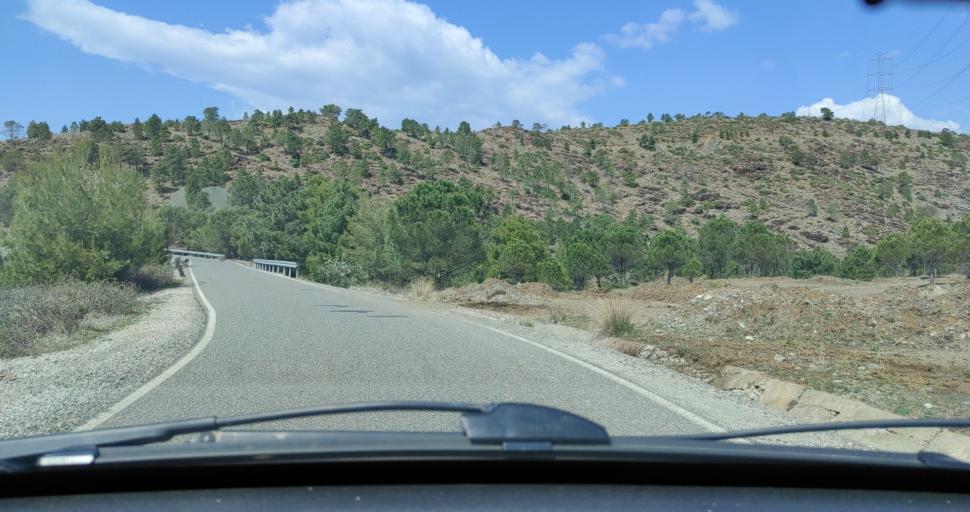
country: AL
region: Shkoder
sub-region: Rrethi i Shkodres
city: Hajmel
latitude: 41.9814
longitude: 19.6470
